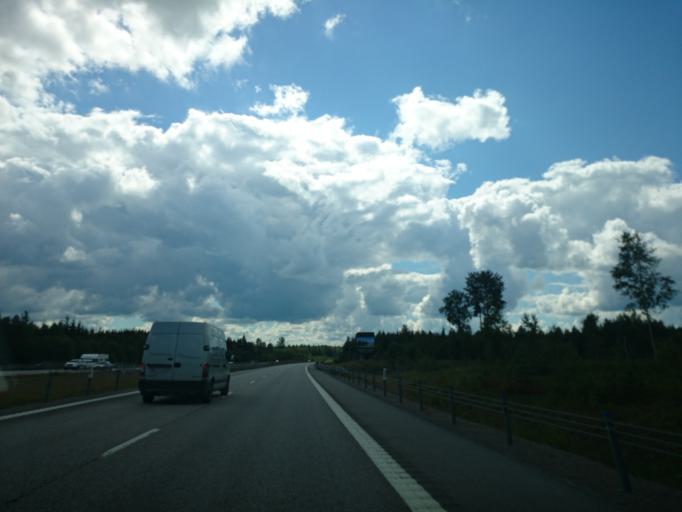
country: SE
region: Uppsala
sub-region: Tierps Kommun
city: Tierp
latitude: 60.3783
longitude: 17.4813
